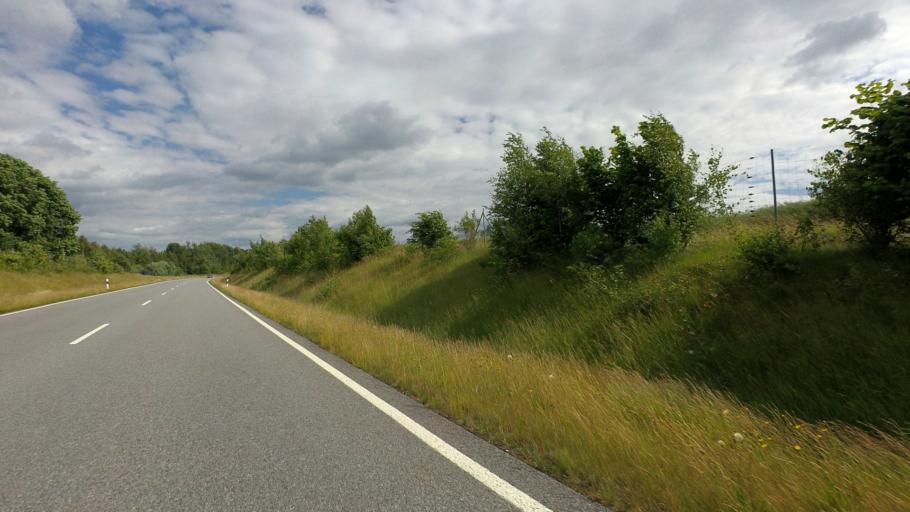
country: DE
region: Saxony
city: Berthelsdorf
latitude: 51.0551
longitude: 14.2057
